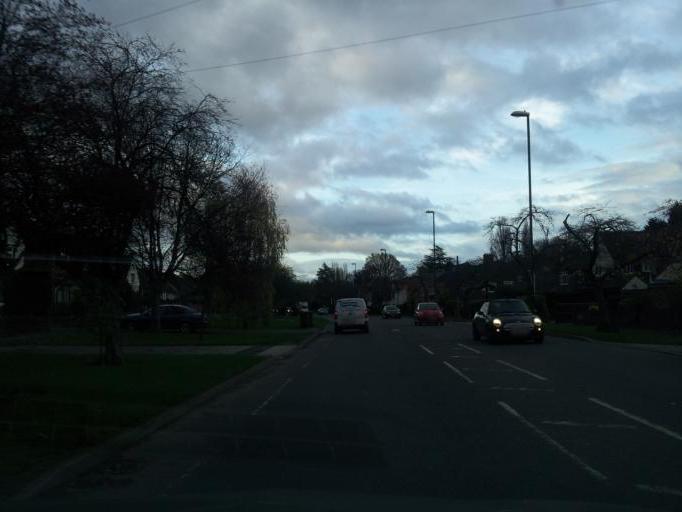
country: GB
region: England
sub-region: Nottinghamshire
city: Kimberley
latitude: 52.9421
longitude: -1.2225
